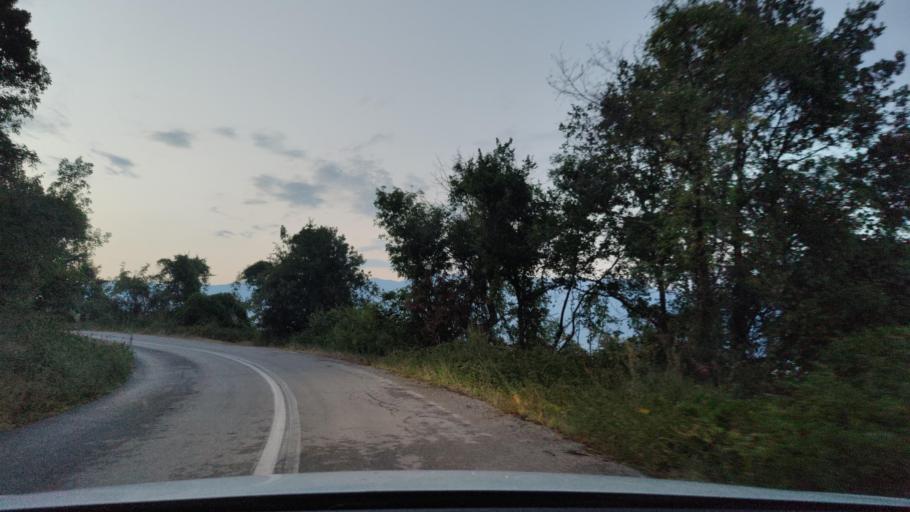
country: GR
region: Central Macedonia
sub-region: Nomos Serron
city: Chrysochorafa
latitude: 41.1776
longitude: 23.1655
